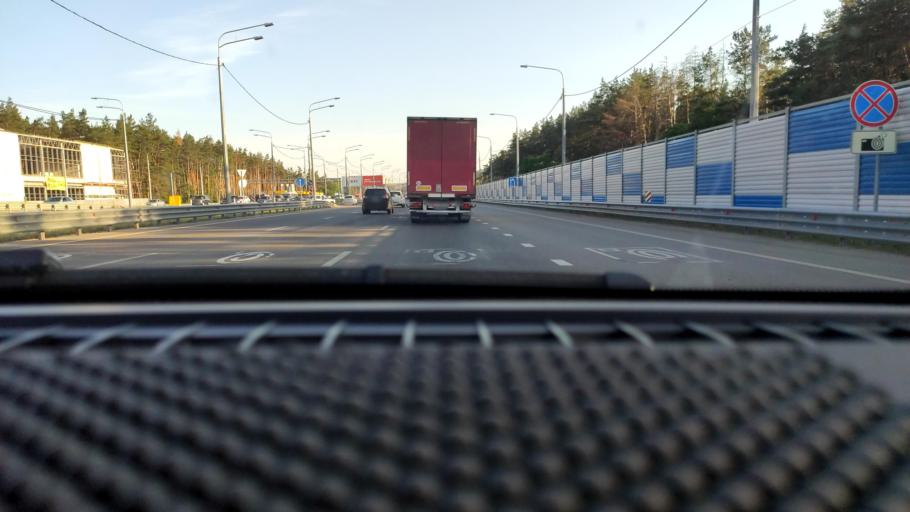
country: RU
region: Voronezj
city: Podgornoye
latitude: 51.7446
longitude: 39.1825
